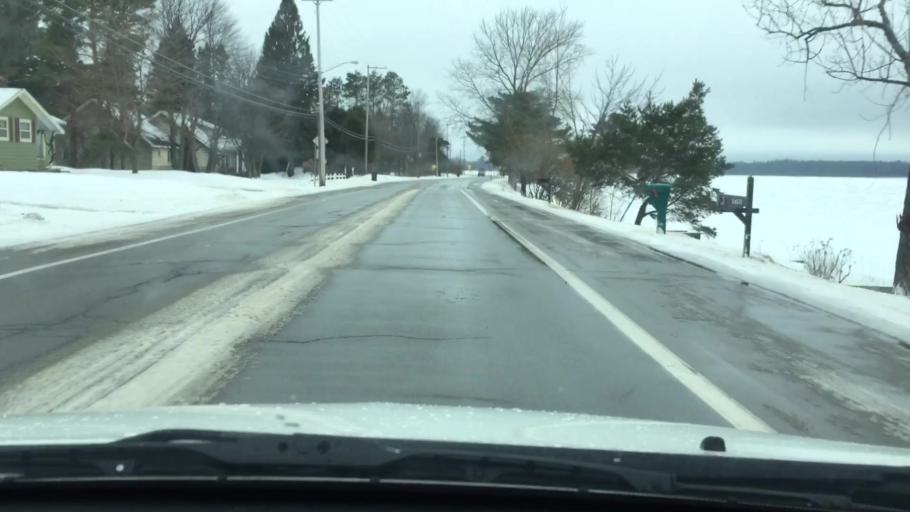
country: US
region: Michigan
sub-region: Wexford County
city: Cadillac
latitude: 44.2342
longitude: -85.4274
